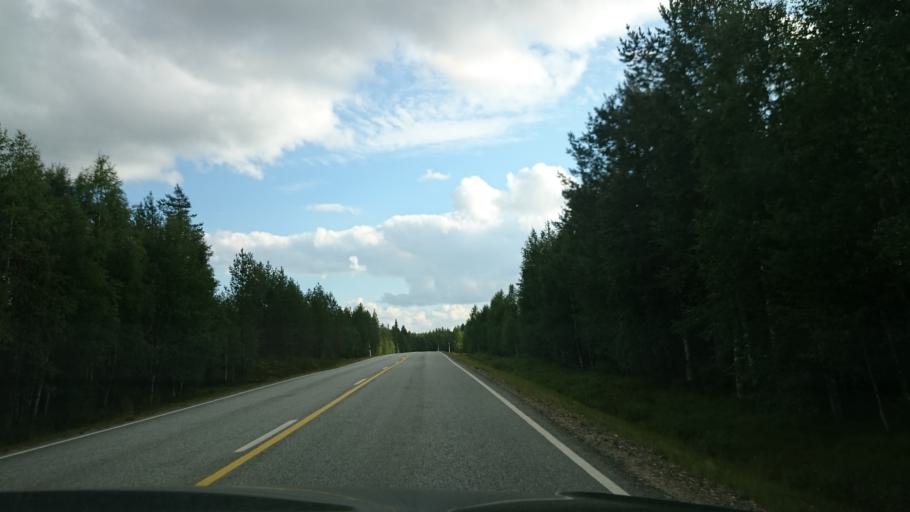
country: FI
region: Kainuu
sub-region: Kehys-Kainuu
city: Kuhmo
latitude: 64.5226
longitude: 29.9459
